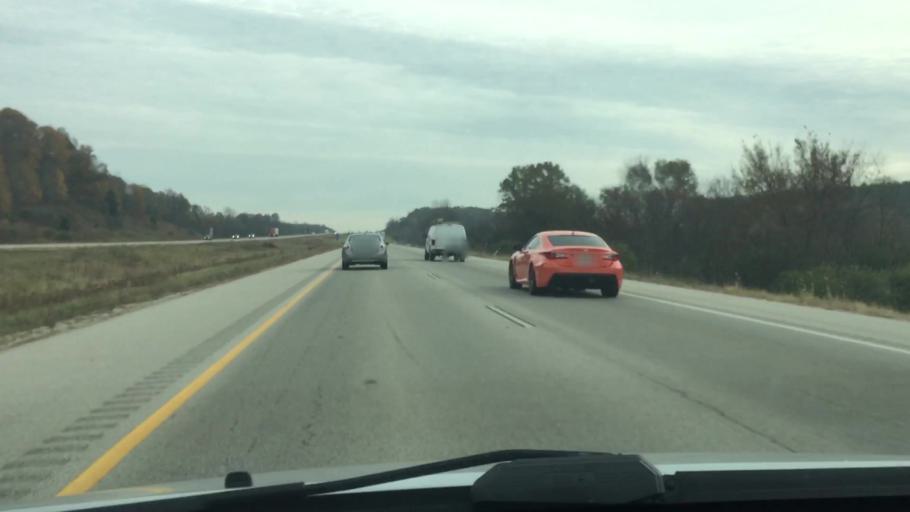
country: US
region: Wisconsin
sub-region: Waukesha County
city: Mukwonago
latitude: 42.8773
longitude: -88.2841
